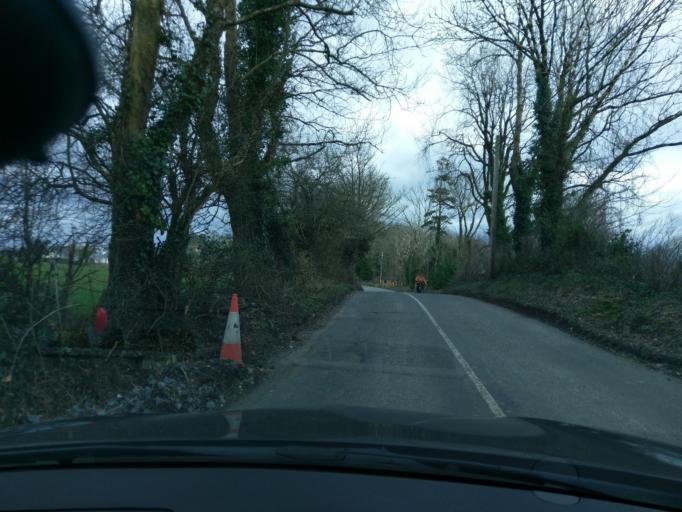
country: IE
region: Connaught
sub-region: County Galway
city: Athenry
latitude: 53.3224
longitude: -8.7086
